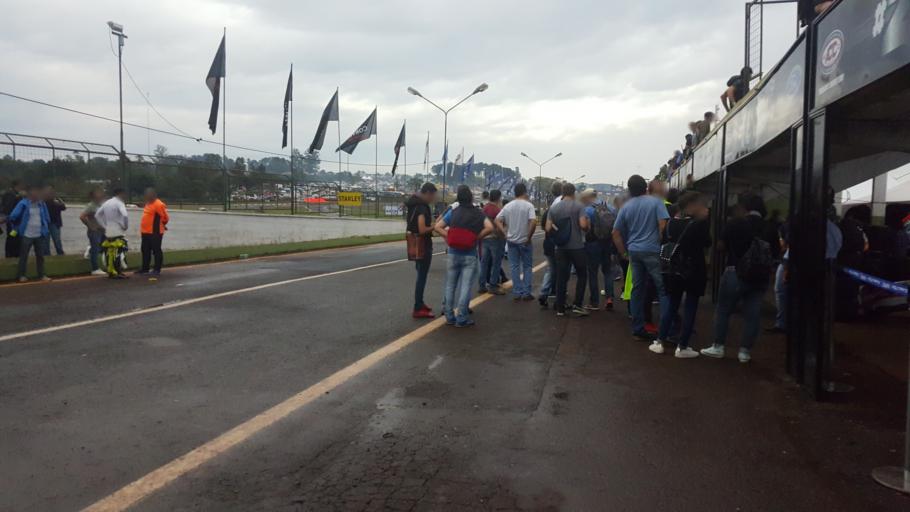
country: AR
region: Misiones
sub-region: Departamento de Capital
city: Posadas
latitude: -27.4400
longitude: -55.9266
